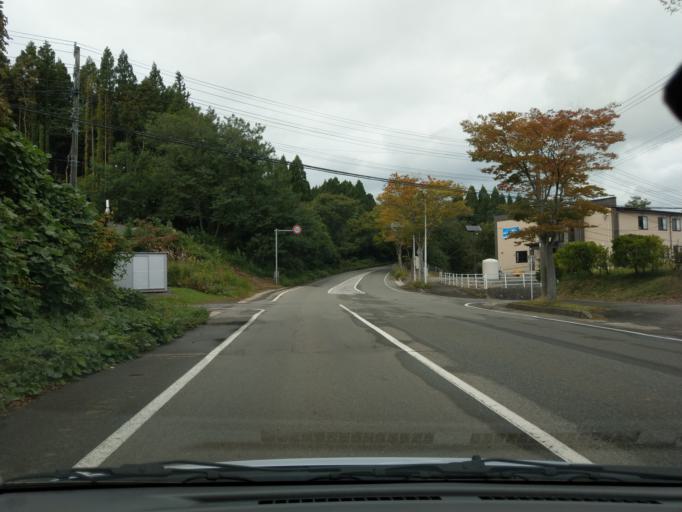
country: JP
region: Akita
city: Akita Shi
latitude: 39.6708
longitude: 140.0819
